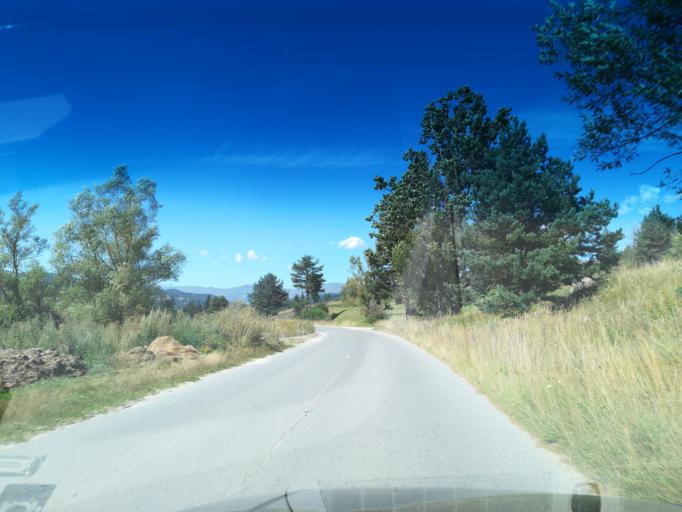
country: BG
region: Sofiya
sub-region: Obshtina Koprivshtitsa
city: Koprivshtitsa
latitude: 42.6093
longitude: 24.3765
